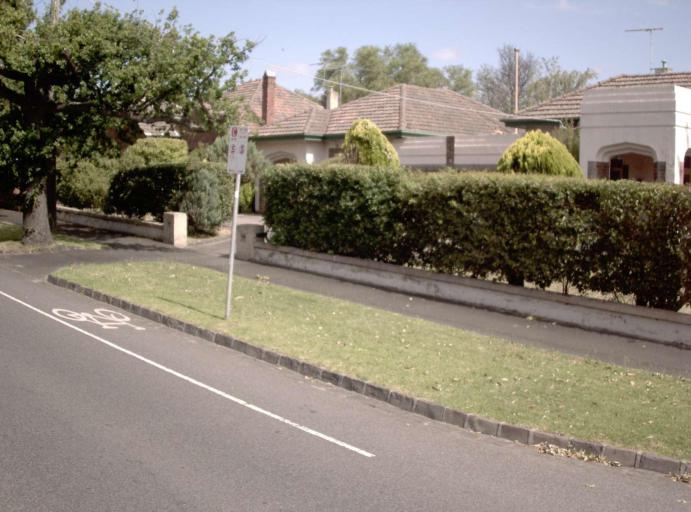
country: AU
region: Victoria
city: Balwyn
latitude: -37.8216
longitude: 145.0605
